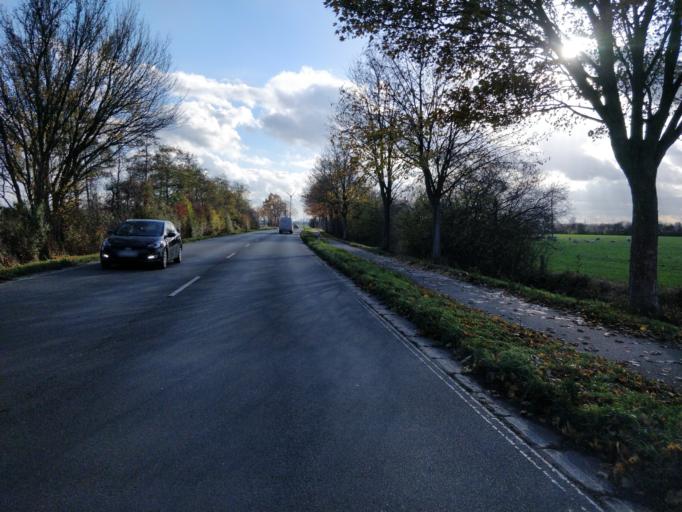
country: DE
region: North Rhine-Westphalia
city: Rees
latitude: 51.7886
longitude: 6.3740
